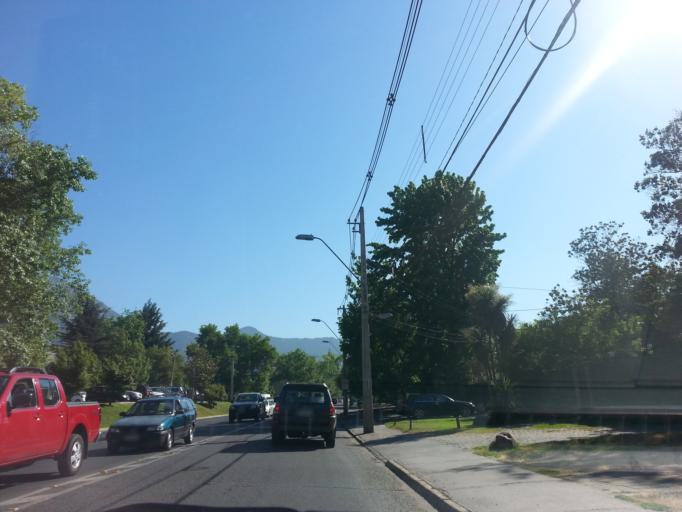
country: CL
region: Santiago Metropolitan
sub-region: Provincia de Santiago
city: Villa Presidente Frei, Nunoa, Santiago, Chile
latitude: -33.3888
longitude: -70.5949
